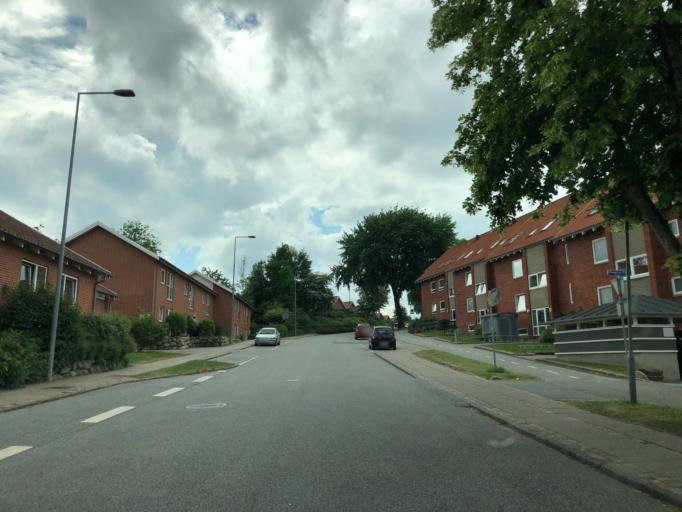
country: DK
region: Central Jutland
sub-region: Struer Kommune
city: Struer
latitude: 56.4903
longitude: 8.5909
